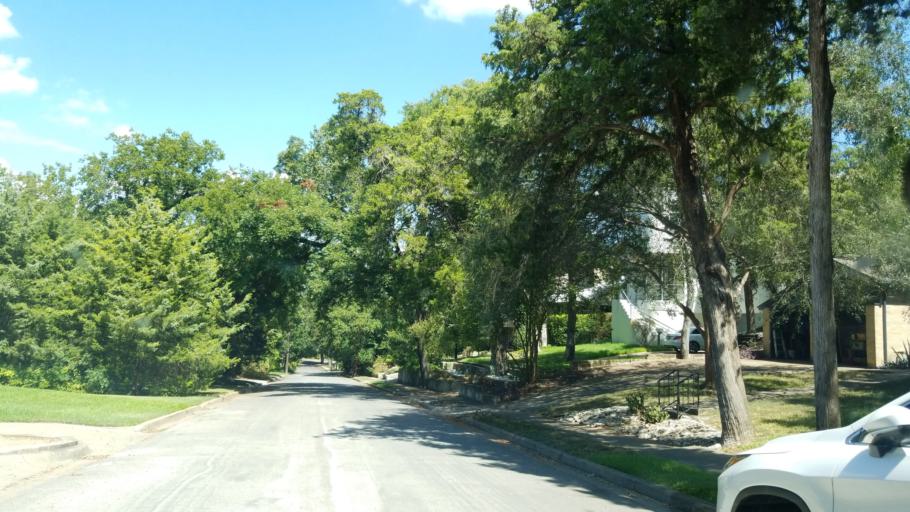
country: US
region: Texas
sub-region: Dallas County
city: Dallas
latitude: 32.7593
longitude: -96.8308
